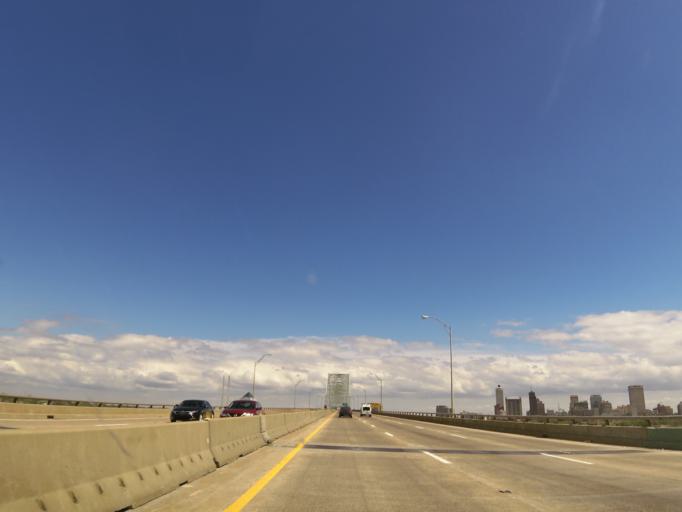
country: US
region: Tennessee
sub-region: Shelby County
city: Memphis
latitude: 35.1532
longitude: -90.0715
